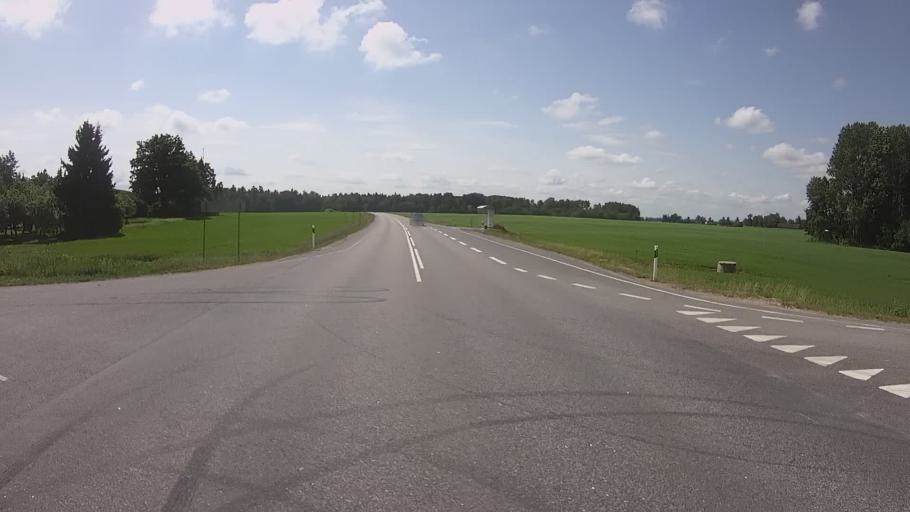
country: EE
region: Tartu
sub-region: Tartu linn
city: Tartu
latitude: 58.3787
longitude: 26.8852
